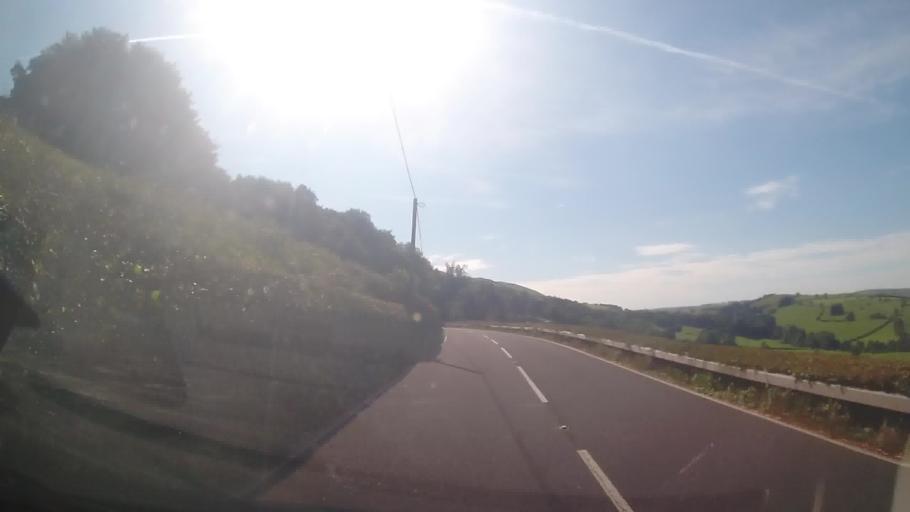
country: GB
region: Wales
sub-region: Sir Powys
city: Mochdre
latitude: 52.4699
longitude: -3.3197
